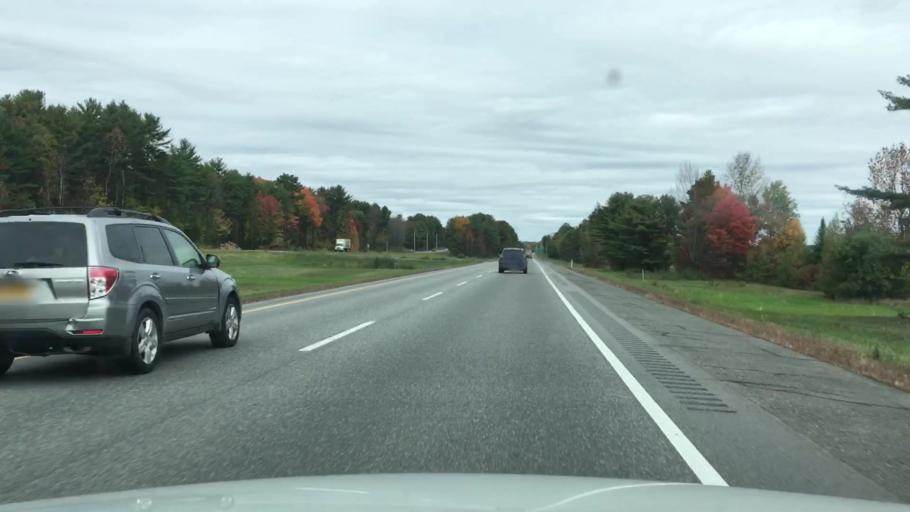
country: US
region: Maine
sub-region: Kennebec County
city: Oakland
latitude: 44.4974
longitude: -69.7042
